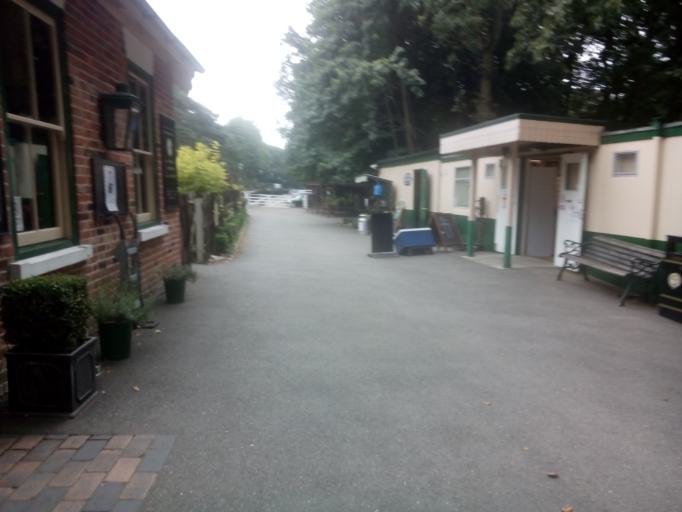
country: GB
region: England
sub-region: Norfolk
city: Briston
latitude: 52.9143
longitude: 1.1133
